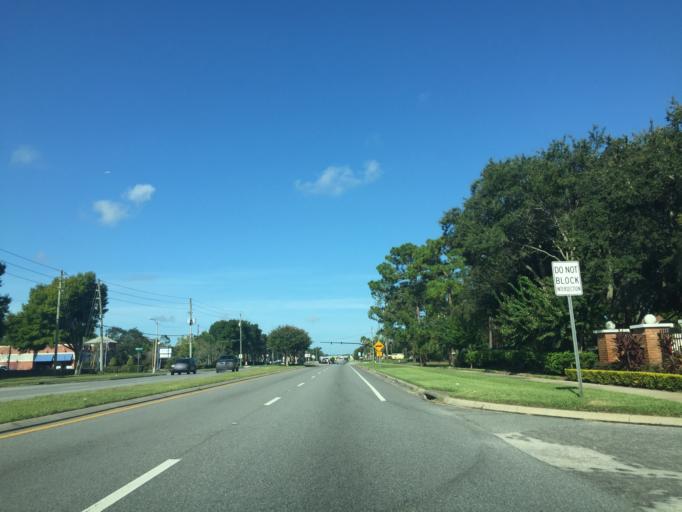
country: US
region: Florida
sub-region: Seminole County
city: Goldenrod
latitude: 28.6477
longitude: -81.2733
